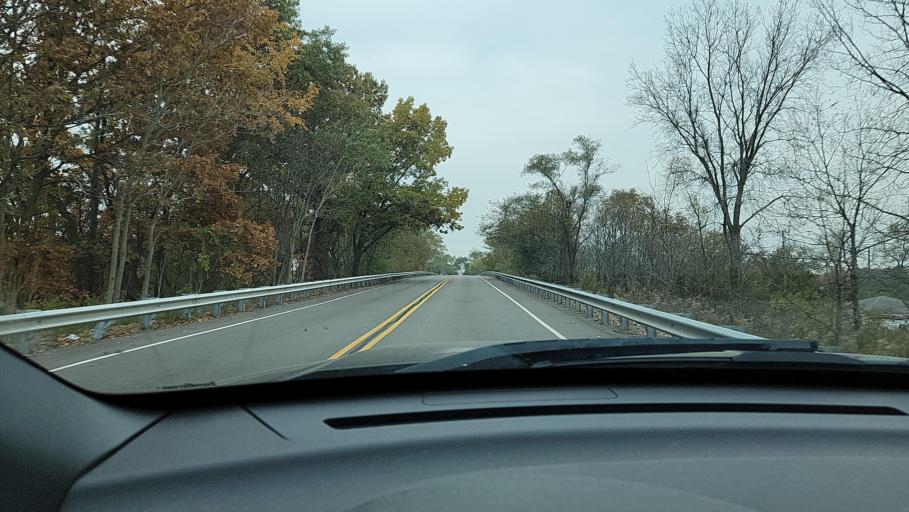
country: US
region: Indiana
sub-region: Lake County
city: Lake Station
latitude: 41.5887
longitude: -87.2125
